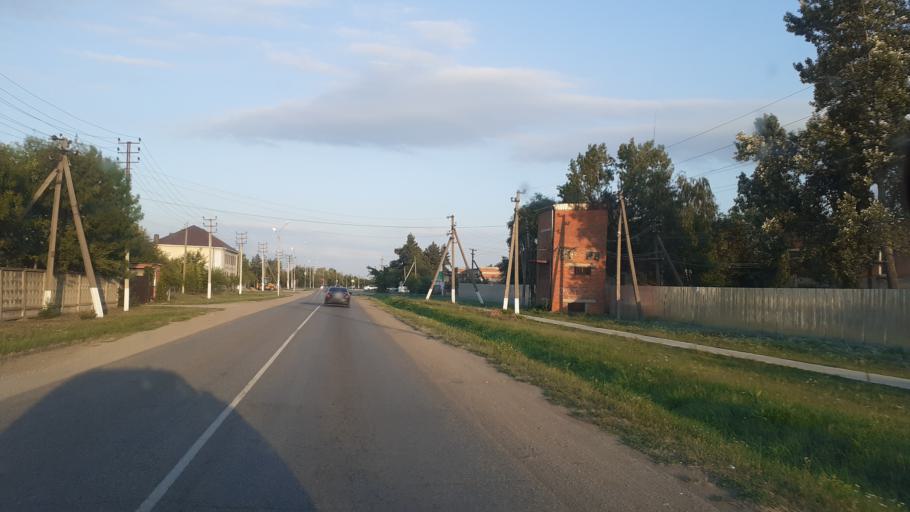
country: RU
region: Krasnodarskiy
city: Severskaya
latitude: 44.8682
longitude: 38.6654
